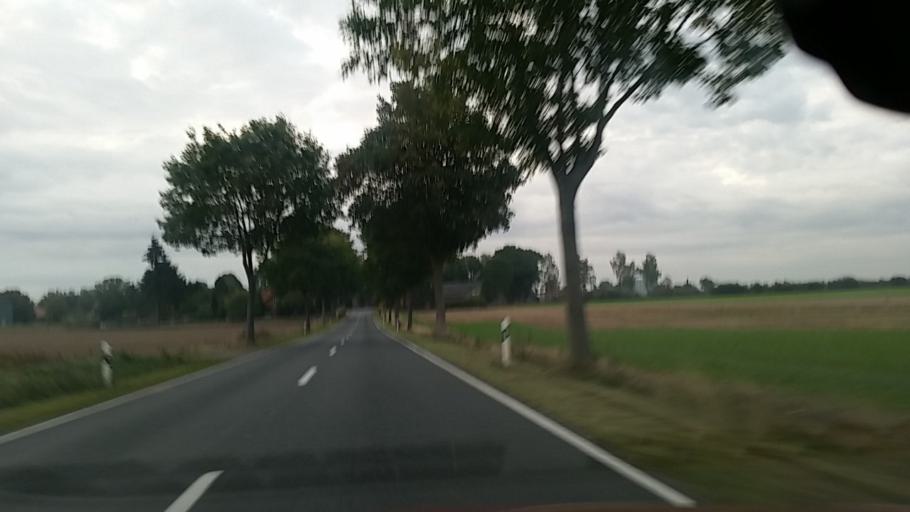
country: DE
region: Lower Saxony
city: Sprakensehl
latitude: 52.7544
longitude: 10.5119
